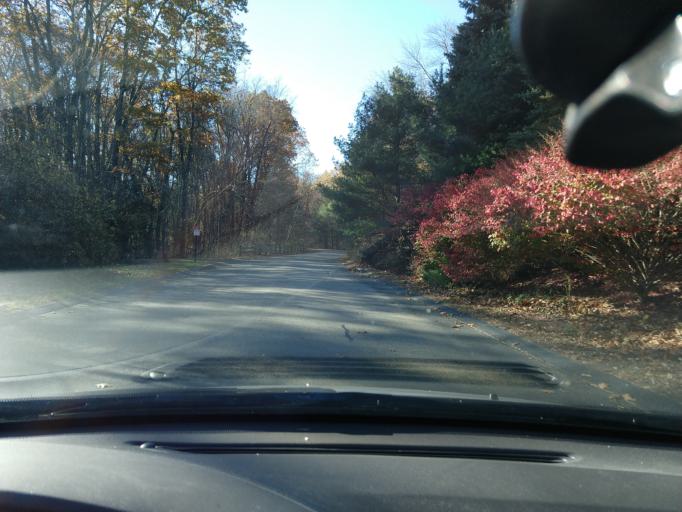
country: US
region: Massachusetts
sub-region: Middlesex County
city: Carlisle
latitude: 42.5006
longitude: -71.3346
